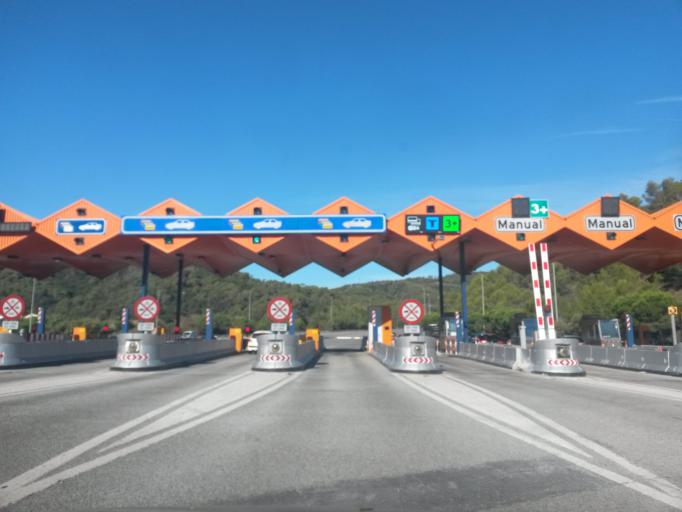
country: ES
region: Catalonia
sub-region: Provincia de Barcelona
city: Pineda de Mar
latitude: 41.6520
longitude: 2.6977
